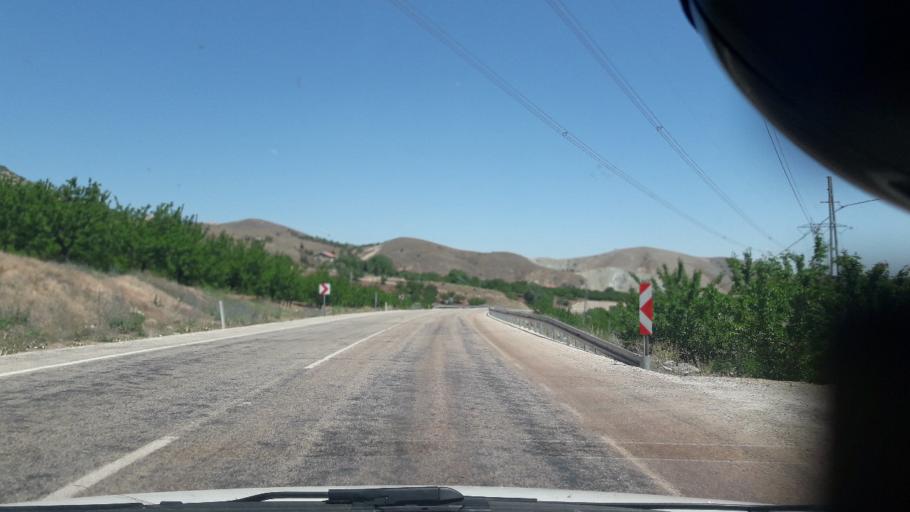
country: TR
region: Malatya
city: Hekimhan
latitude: 38.8402
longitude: 37.8386
